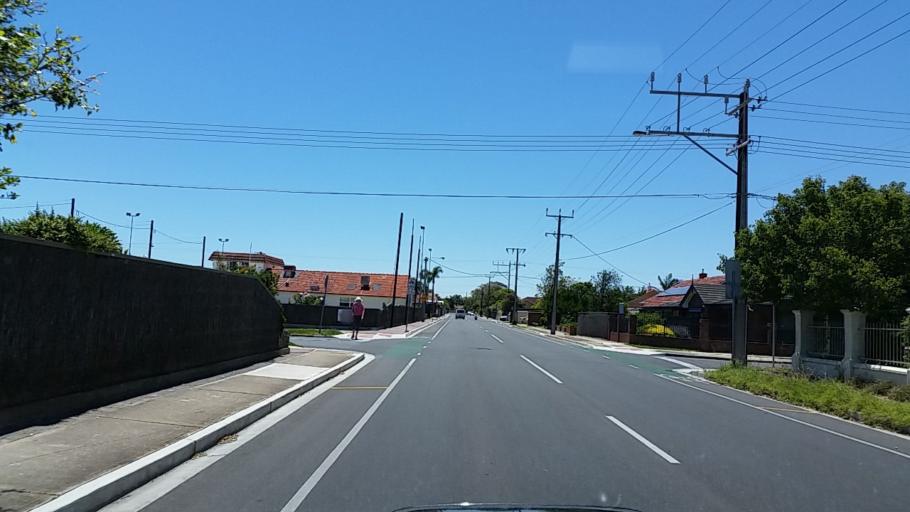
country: AU
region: South Australia
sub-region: Holdfast Bay
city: North Brighton
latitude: -35.0006
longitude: 138.5173
